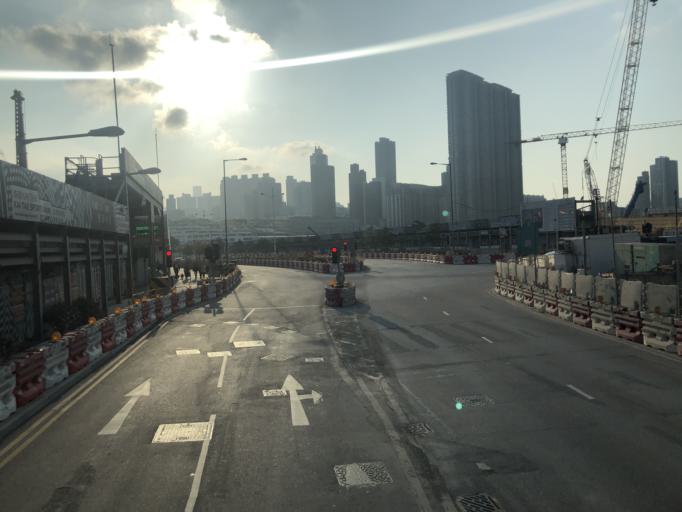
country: HK
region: Kowloon City
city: Kowloon
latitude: 22.3237
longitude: 114.1964
